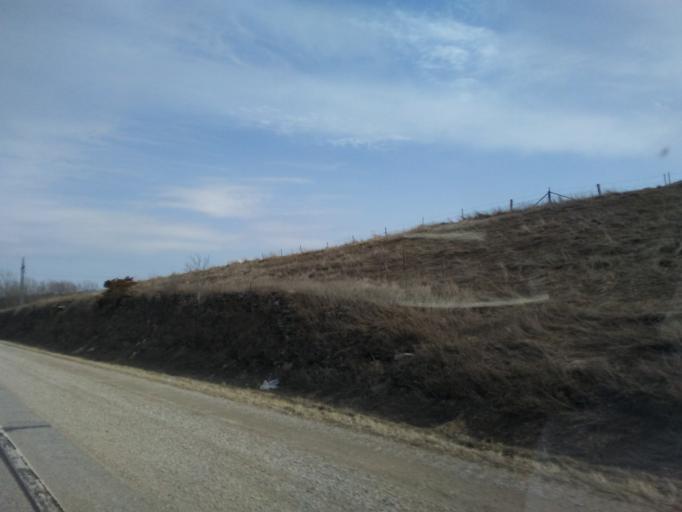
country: US
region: Iowa
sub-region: Allamakee County
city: Waukon
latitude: 43.2405
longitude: -91.5202
